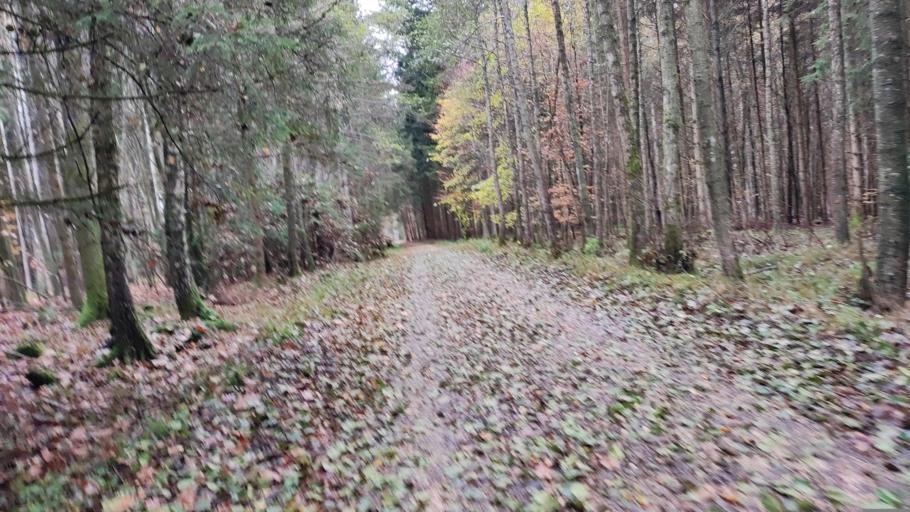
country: DE
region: Bavaria
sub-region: Swabia
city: Burtenbach
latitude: 48.3375
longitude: 10.4965
